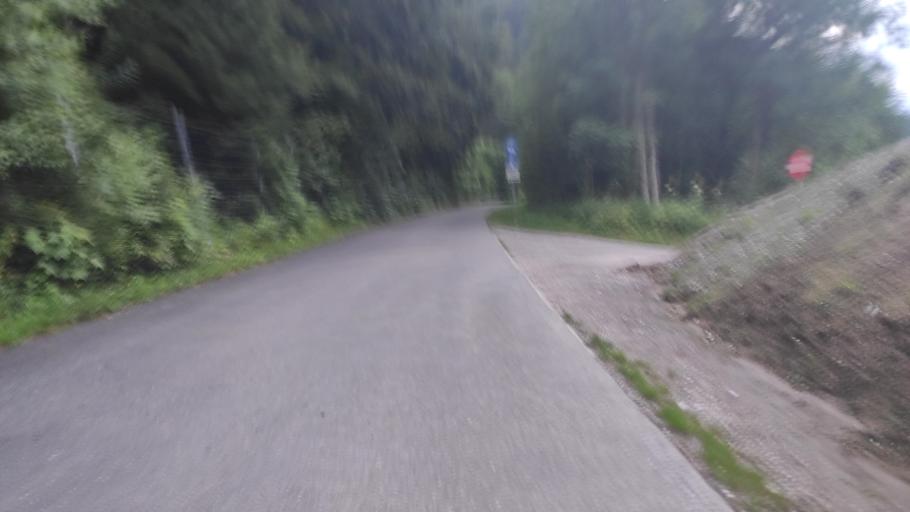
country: AT
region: Salzburg
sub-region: Politischer Bezirk Zell am See
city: Saalfelden am Steinernen Meer
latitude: 47.4796
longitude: 12.8340
